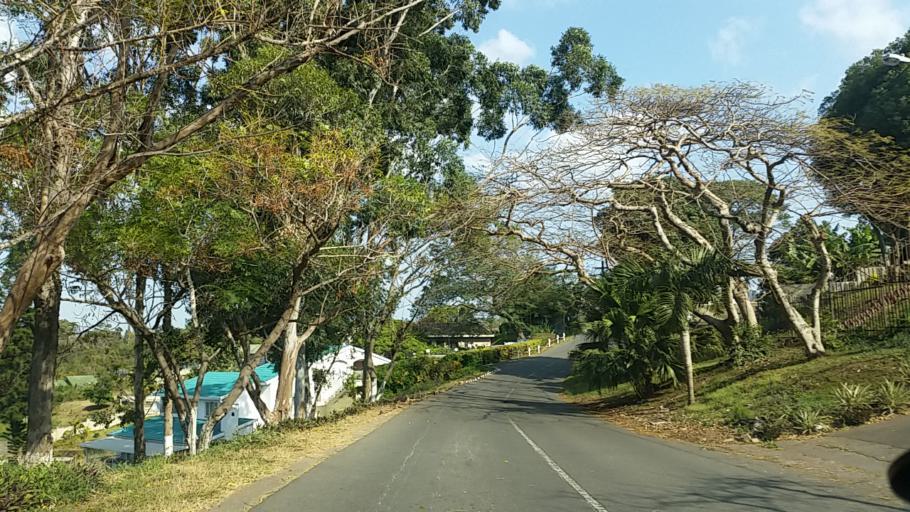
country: ZA
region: KwaZulu-Natal
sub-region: eThekwini Metropolitan Municipality
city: Berea
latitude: -29.8342
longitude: 30.9561
